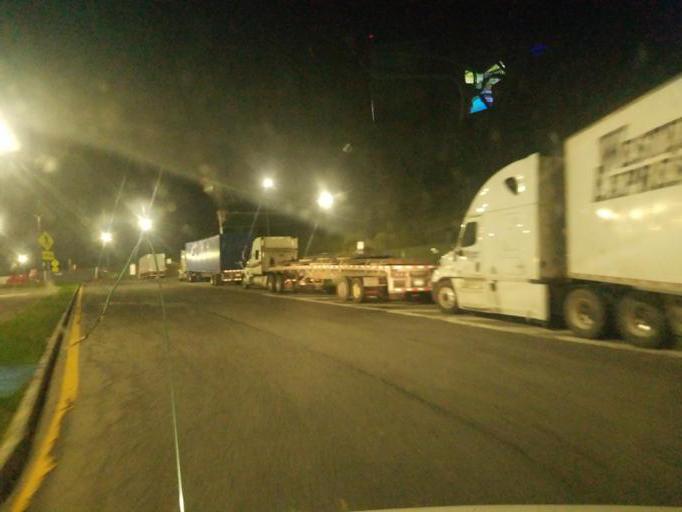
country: US
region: New York
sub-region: Montgomery County
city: Amsterdam
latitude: 42.9146
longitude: -74.1636
